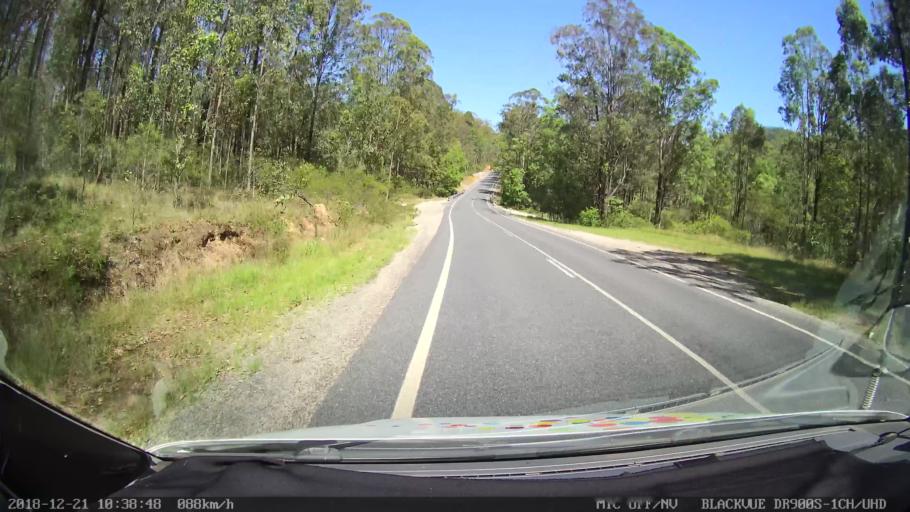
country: AU
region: New South Wales
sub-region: Clarence Valley
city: Gordon
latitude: -29.6118
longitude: 152.6054
